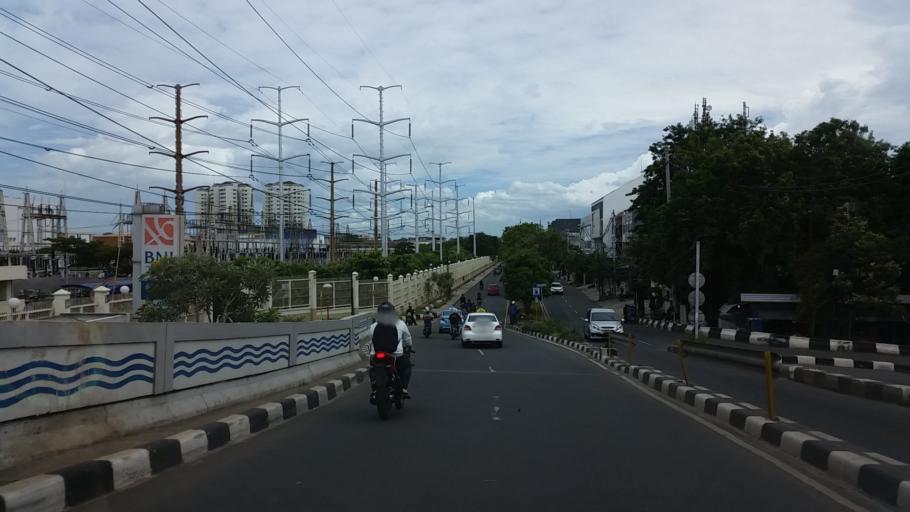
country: ID
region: Jakarta Raya
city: Jakarta
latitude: -6.1123
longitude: 106.7850
